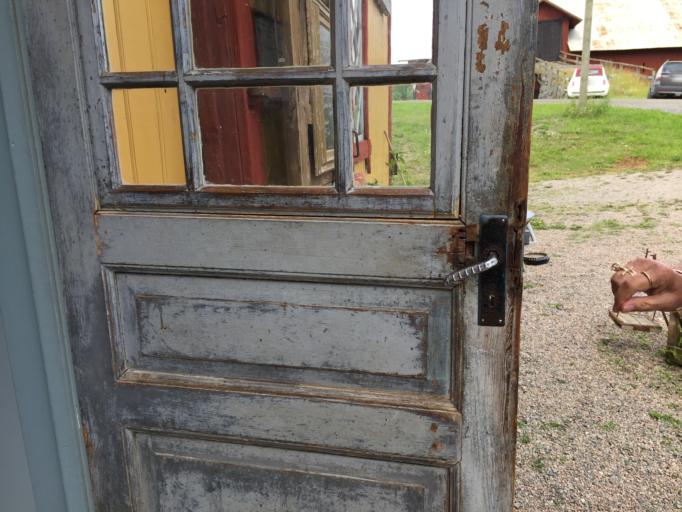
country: SE
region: Soedermanland
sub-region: Katrineholms Kommun
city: Katrineholm
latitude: 59.2063
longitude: 16.2336
